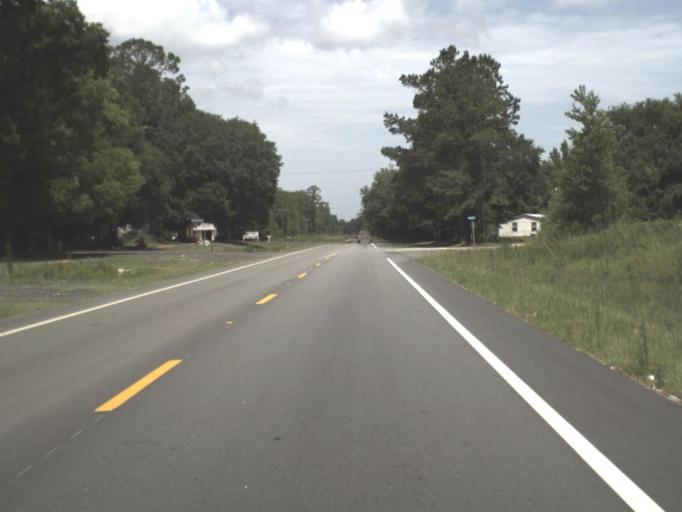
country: US
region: Florida
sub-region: Jefferson County
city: Monticello
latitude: 30.4757
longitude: -83.6681
